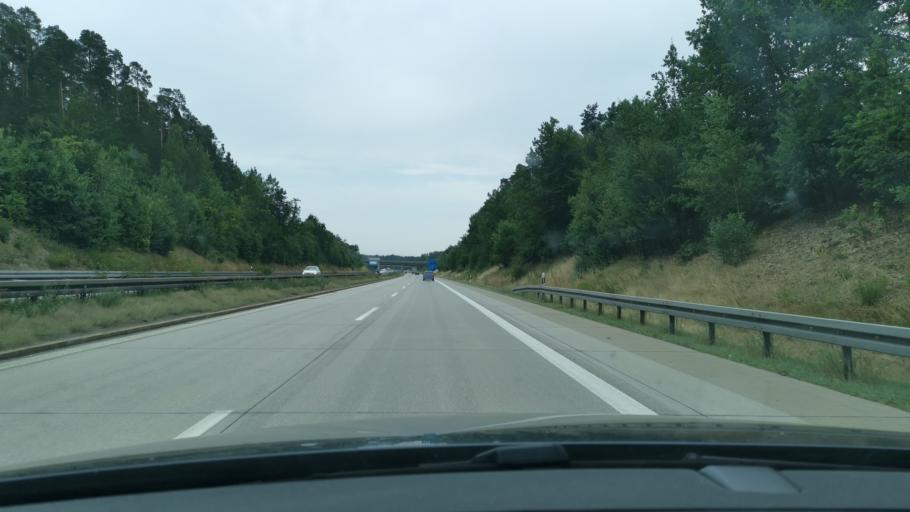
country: DE
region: Bavaria
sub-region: Upper Palatinate
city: Wernberg-Koblitz
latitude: 49.5459
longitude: 12.1289
